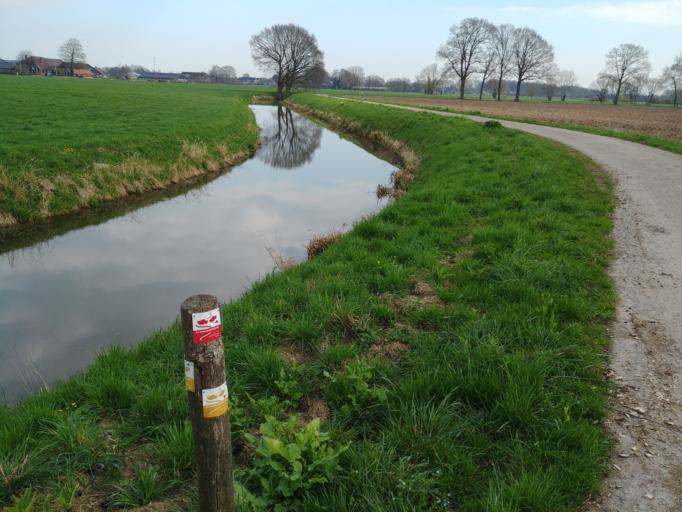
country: NL
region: Gelderland
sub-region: Gemeente Voorst
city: Twello
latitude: 52.2827
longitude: 6.0839
